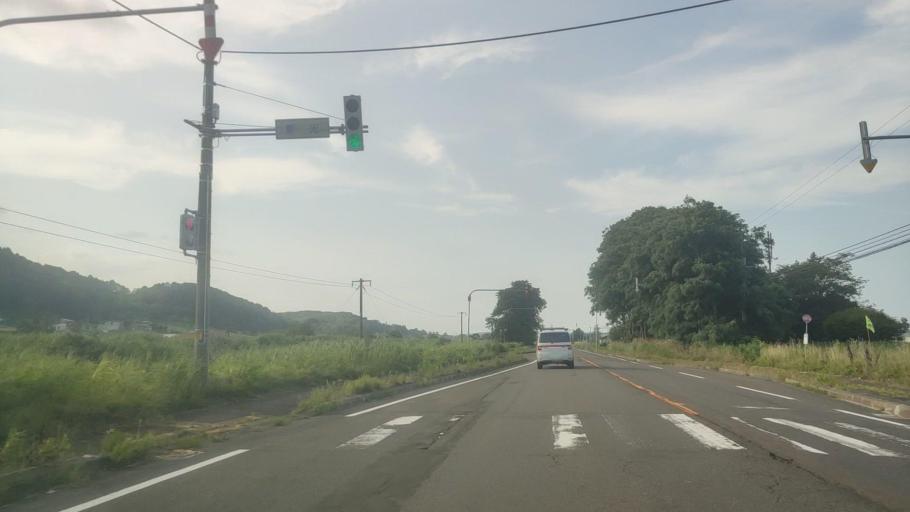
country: JP
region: Hokkaido
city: Iwamizawa
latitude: 42.9993
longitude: 141.7891
